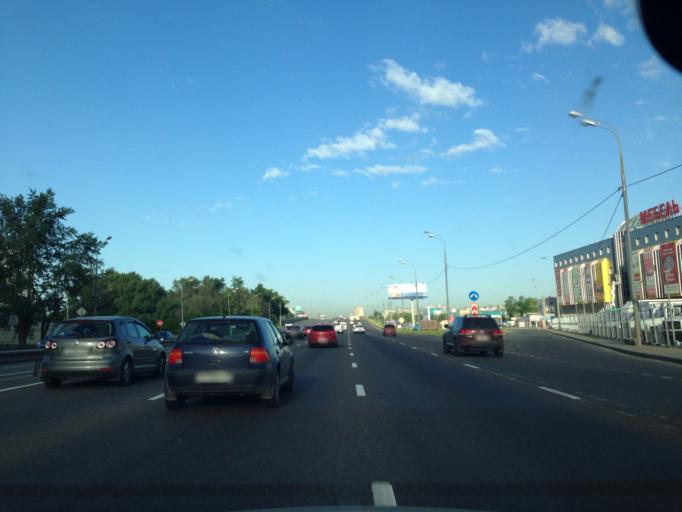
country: RU
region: Moskovskaya
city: Reutov
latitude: 55.7836
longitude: 37.8705
